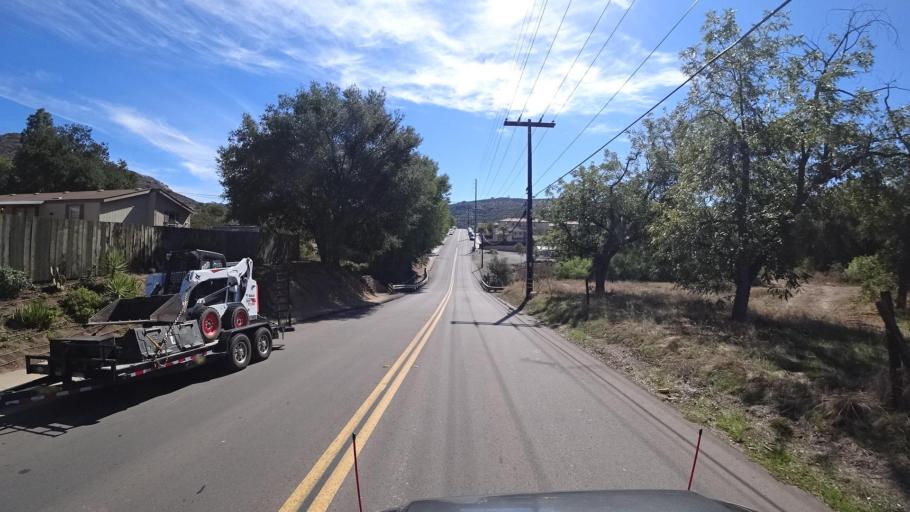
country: US
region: California
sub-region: San Diego County
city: Crest
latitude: 32.8433
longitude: -116.8772
